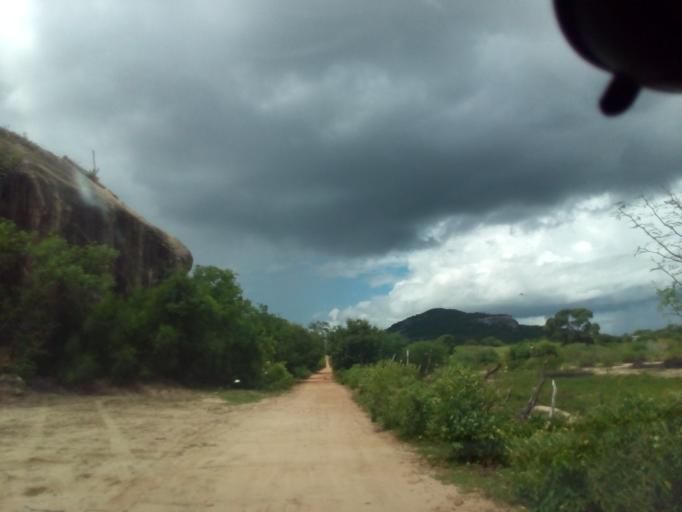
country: BR
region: Rio Grande do Norte
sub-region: Sao Tome
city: Sao Tome
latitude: -5.9520
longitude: -35.9203
